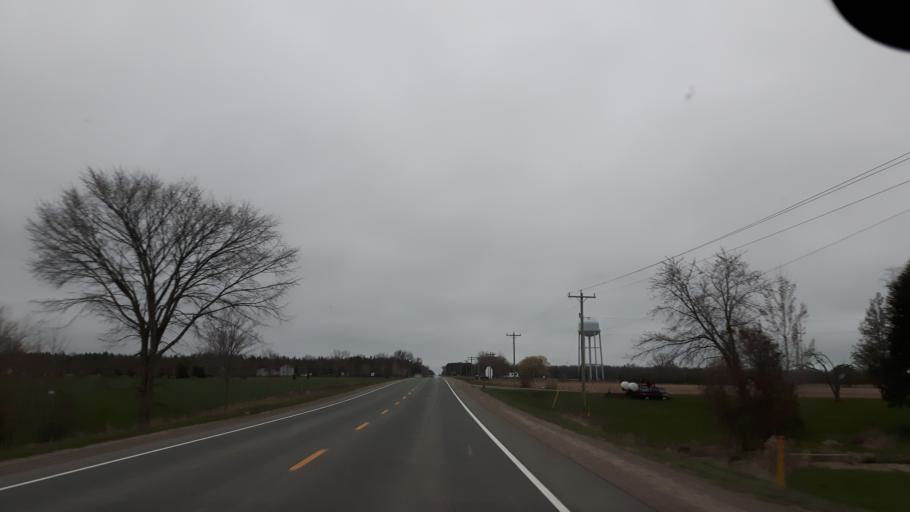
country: CA
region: Ontario
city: Goderich
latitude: 43.6935
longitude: -81.7057
